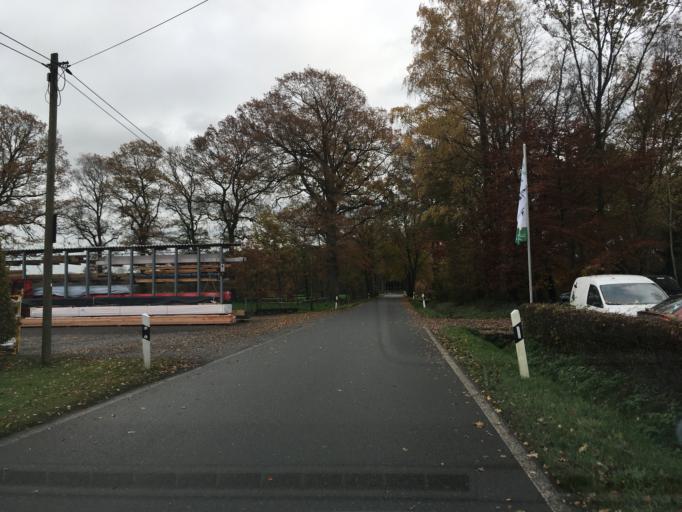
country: DE
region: North Rhine-Westphalia
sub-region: Regierungsbezirk Munster
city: Gescher
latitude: 51.9858
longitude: 6.9763
